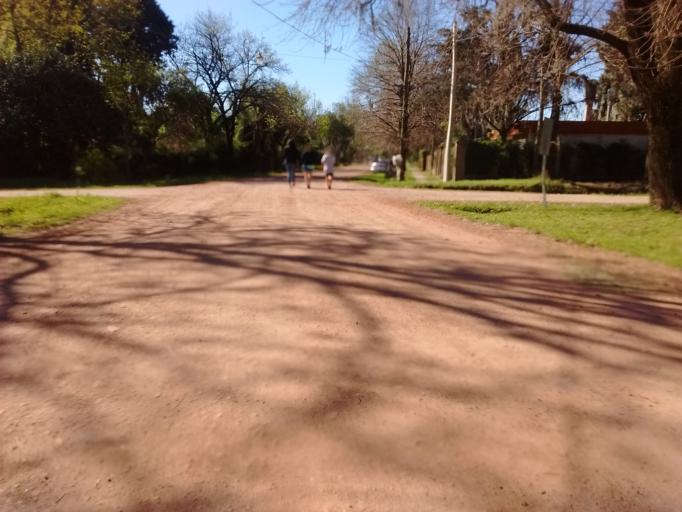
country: AR
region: Santa Fe
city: Funes
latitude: -32.9238
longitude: -60.8140
